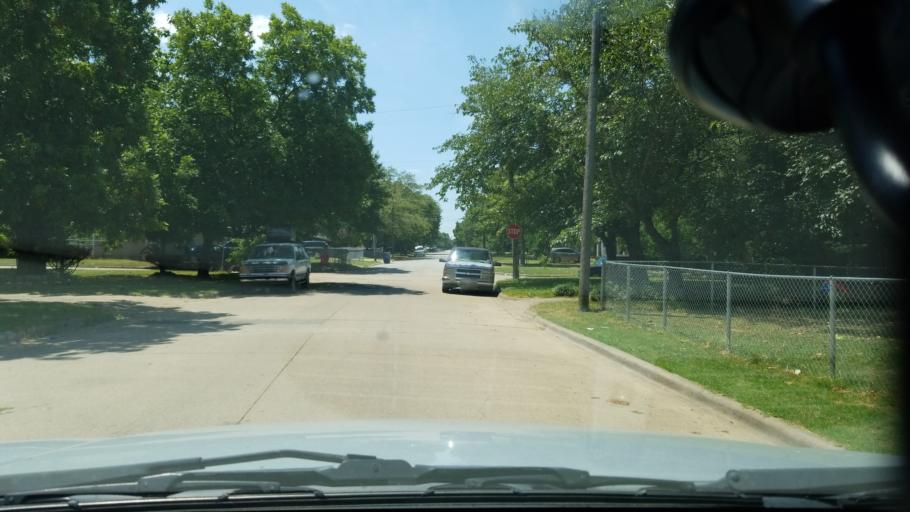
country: US
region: Texas
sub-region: Dallas County
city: Grand Prairie
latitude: 32.7585
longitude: -96.9569
